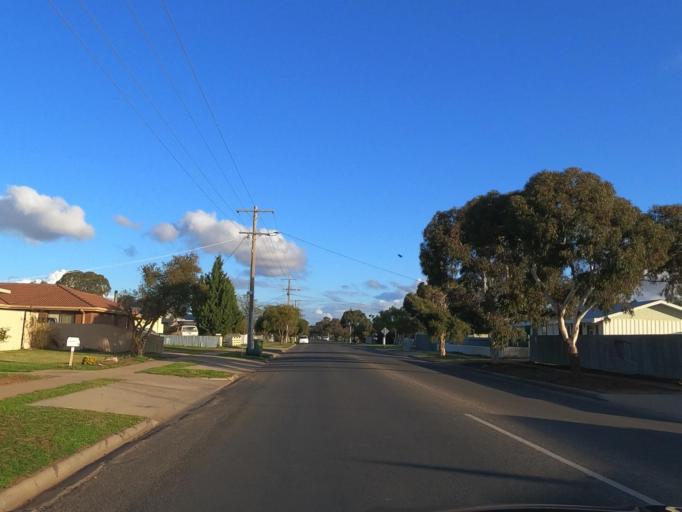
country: AU
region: Victoria
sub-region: Swan Hill
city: Swan Hill
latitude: -35.3406
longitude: 143.5442
